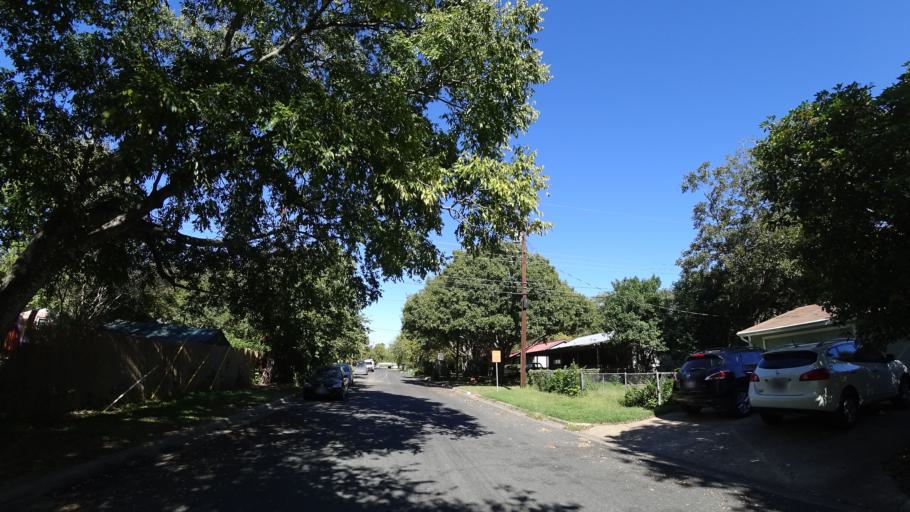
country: US
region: Texas
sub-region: Travis County
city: Rollingwood
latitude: 30.2256
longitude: -97.7880
